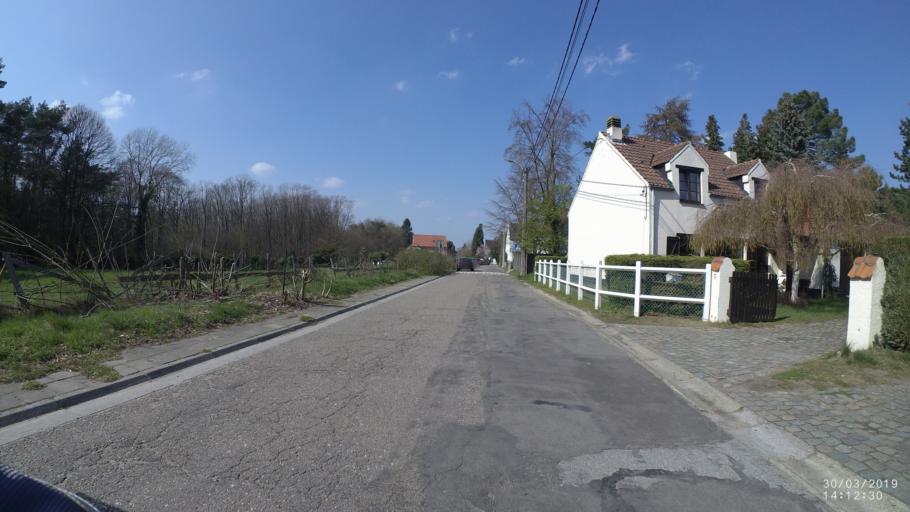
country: BE
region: Wallonia
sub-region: Province du Brabant Wallon
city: Ottignies
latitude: 50.6863
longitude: 4.5839
